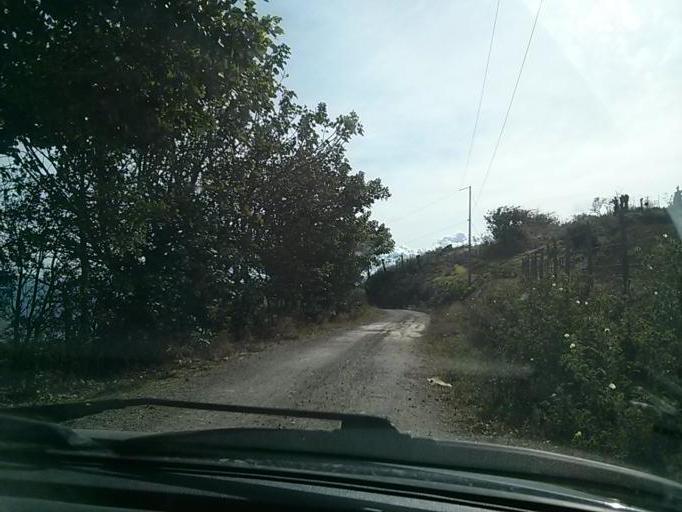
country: CR
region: Cartago
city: Cot
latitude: 9.9134
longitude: -83.9085
